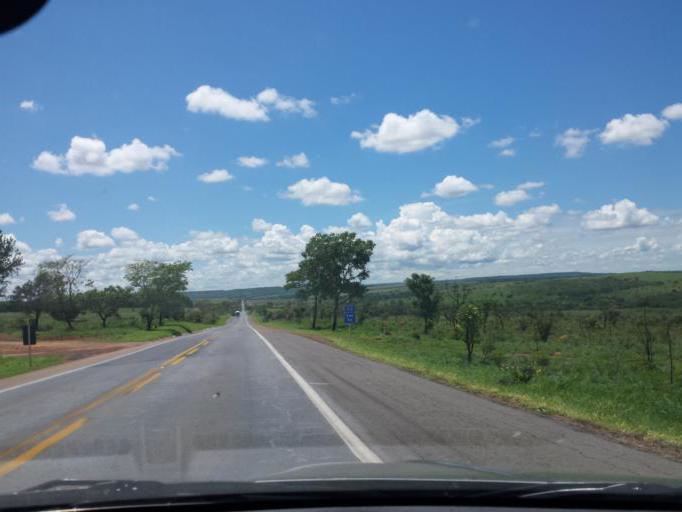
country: BR
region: Goias
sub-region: Cristalina
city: Cristalina
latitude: -16.5724
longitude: -47.7887
